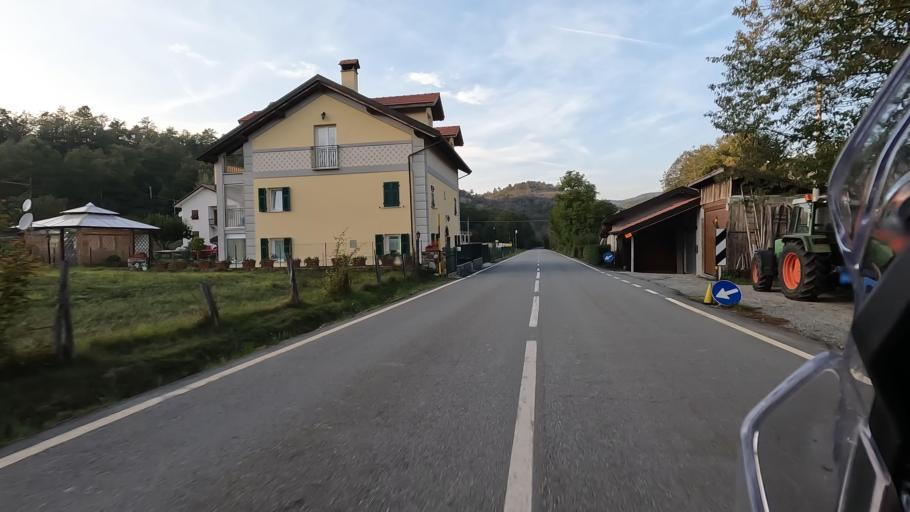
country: IT
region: Liguria
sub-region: Provincia di Savona
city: Sassello
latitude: 44.5123
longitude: 8.4738
